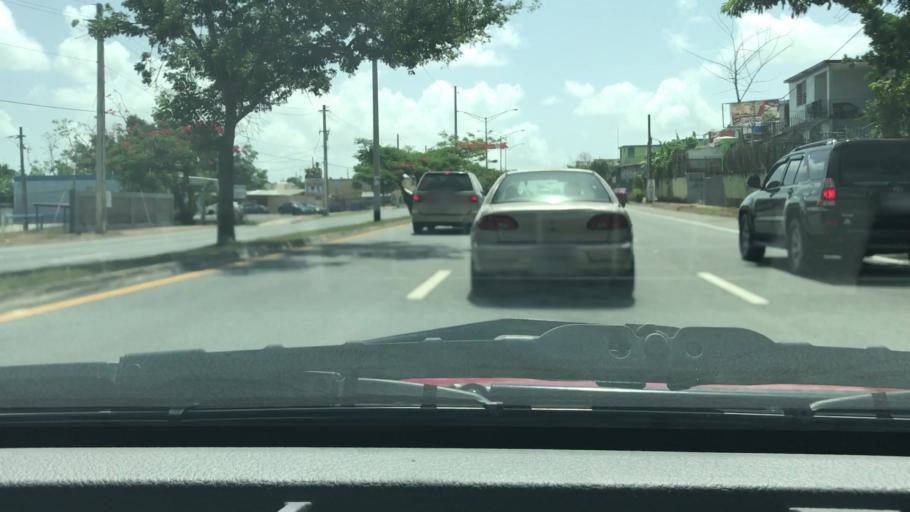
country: PR
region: Toa Alta
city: Pajaros
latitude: 18.3647
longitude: -66.1783
